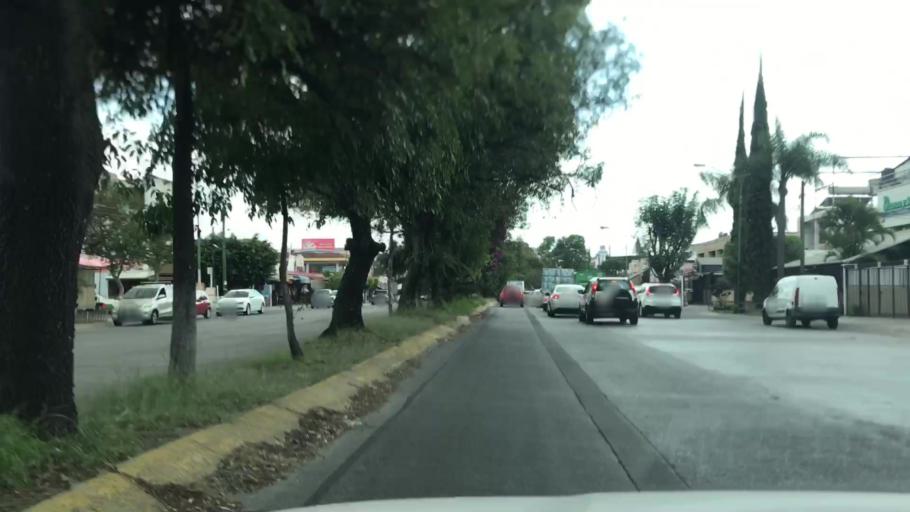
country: MX
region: Jalisco
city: Guadalajara
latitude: 20.6360
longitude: -103.4274
